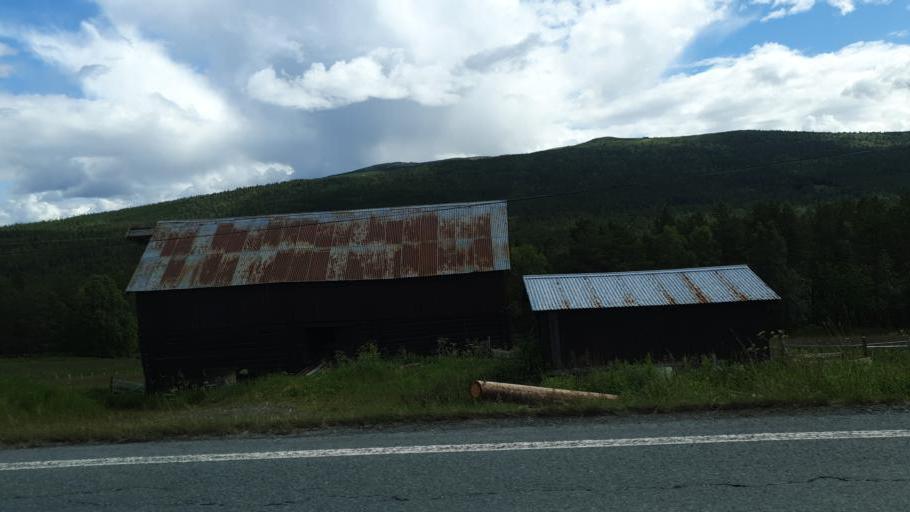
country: NO
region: Sor-Trondelag
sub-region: Rennebu
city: Berkak
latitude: 62.6785
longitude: 9.9209
